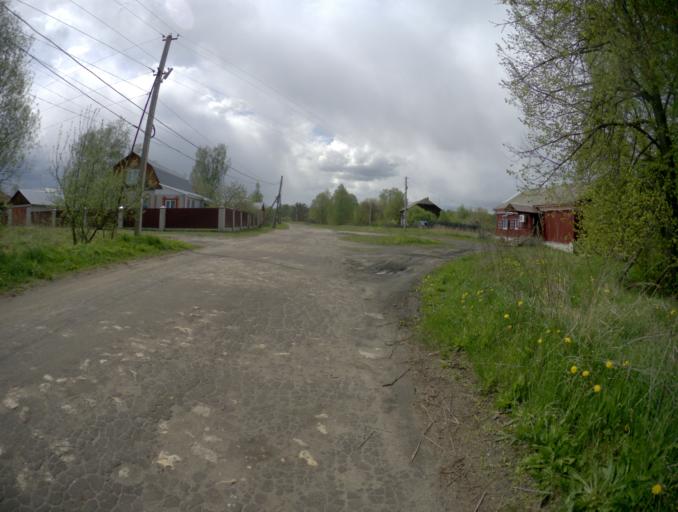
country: RU
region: Vladimir
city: Velikodvorskiy
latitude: 55.2411
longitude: 40.6600
